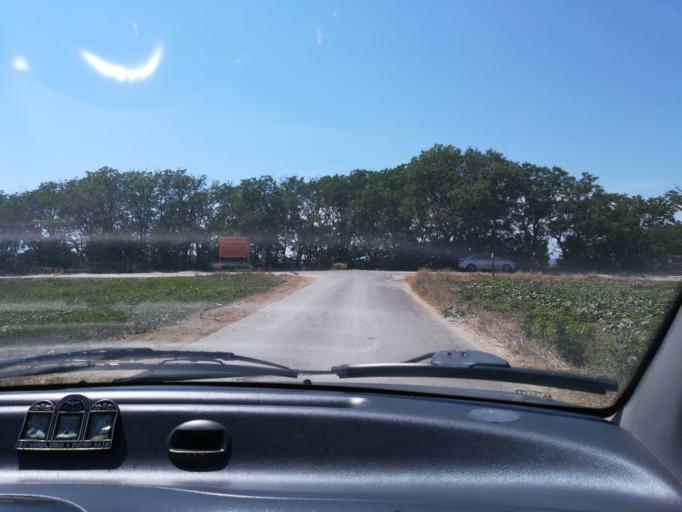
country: RU
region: Krasnodarskiy
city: Blagovetschenskaya
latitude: 45.0683
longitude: 37.0559
